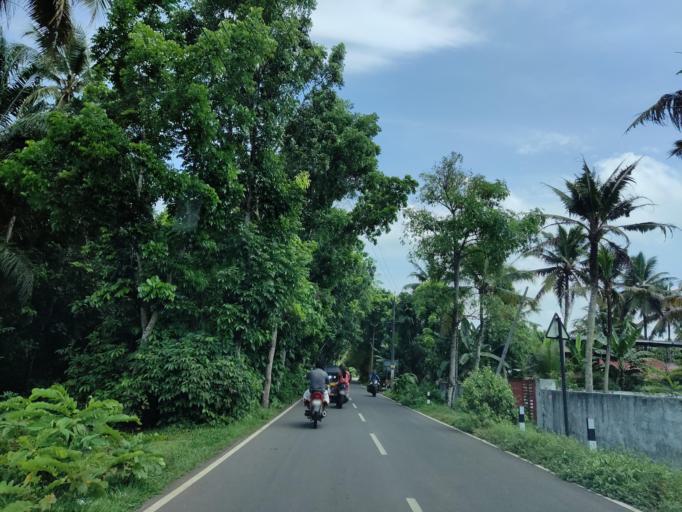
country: IN
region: Kerala
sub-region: Alappuzha
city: Mavelikara
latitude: 9.2940
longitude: 76.5720
